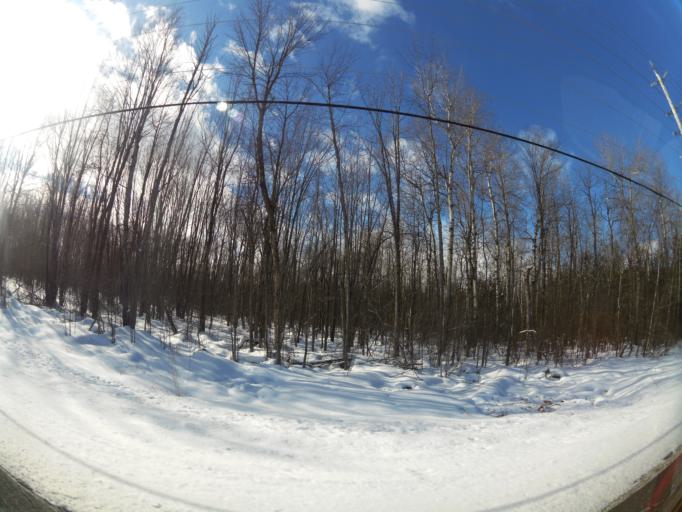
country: CA
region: Ontario
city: Ottawa
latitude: 45.2618
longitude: -75.5144
